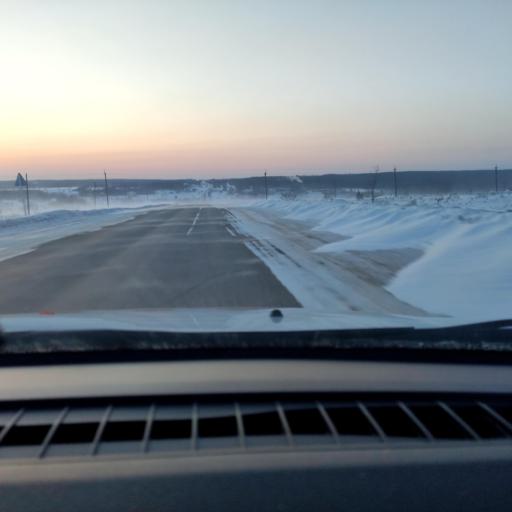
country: RU
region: Samara
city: Georgiyevka
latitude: 53.4179
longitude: 50.8627
